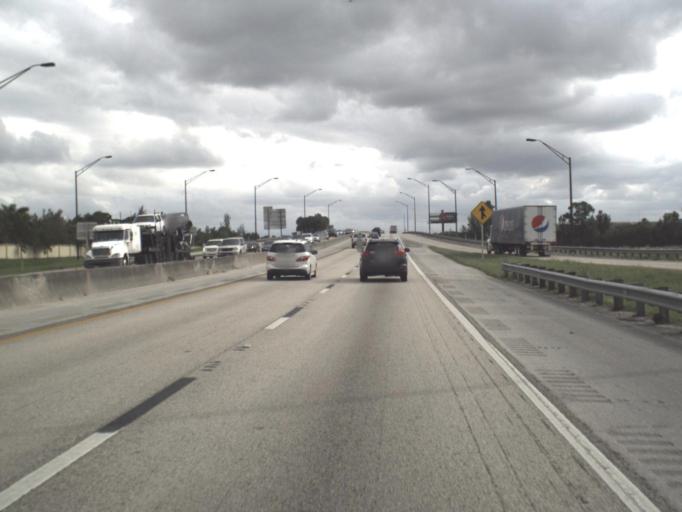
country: US
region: Florida
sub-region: Palm Beach County
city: Palm Beach Gardens
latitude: 26.8002
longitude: -80.1316
